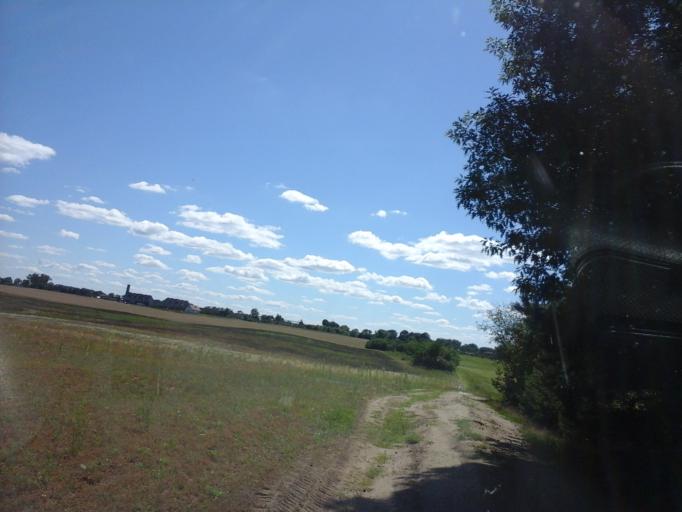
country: PL
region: West Pomeranian Voivodeship
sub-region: Powiat choszczenski
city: Drawno
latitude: 53.2621
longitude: 15.7183
